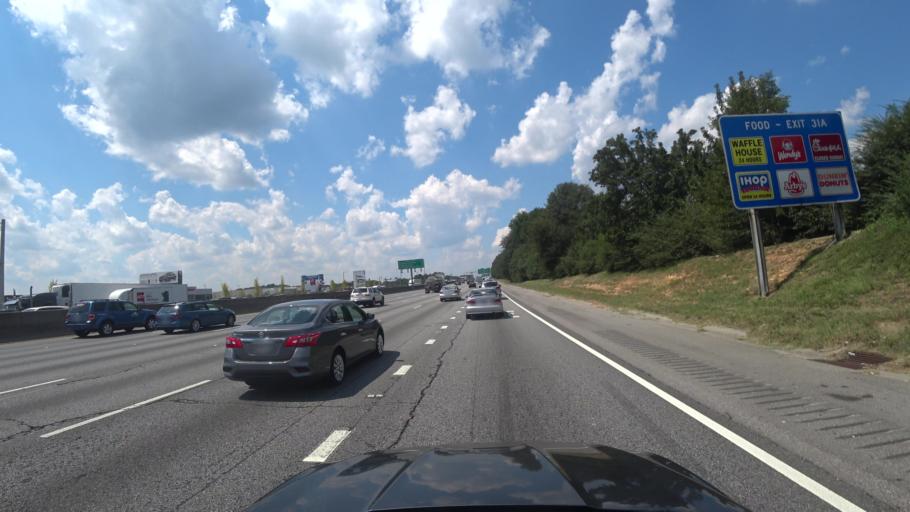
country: US
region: Georgia
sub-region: DeKalb County
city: Doraville
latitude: 33.9076
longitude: -84.2805
